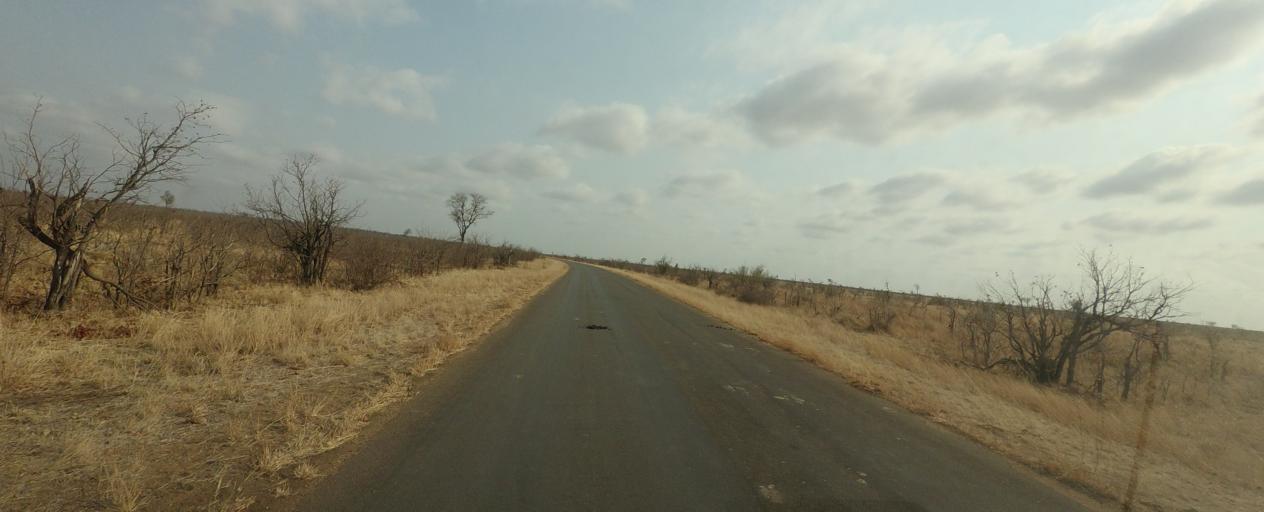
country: ZA
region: Limpopo
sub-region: Vhembe District Municipality
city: Mutale
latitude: -22.9027
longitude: 31.2530
